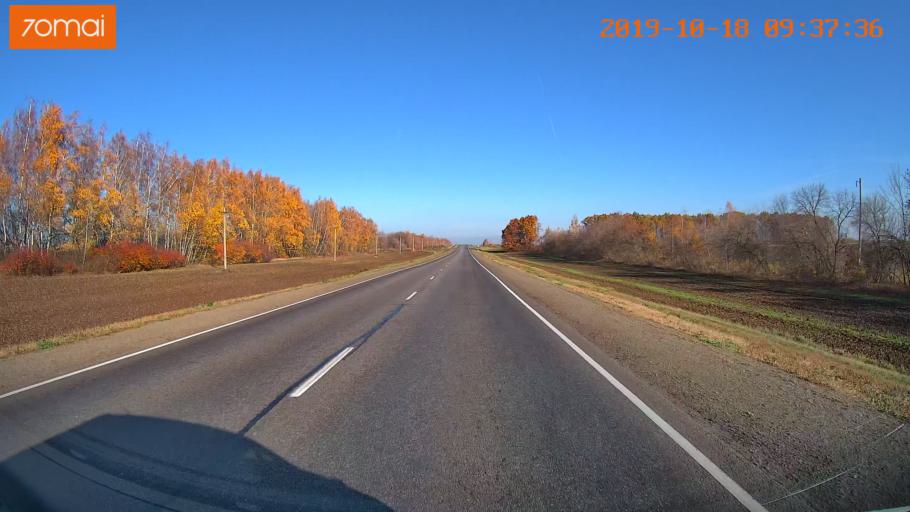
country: RU
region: Tula
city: Yefremov
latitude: 53.2250
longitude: 38.1404
